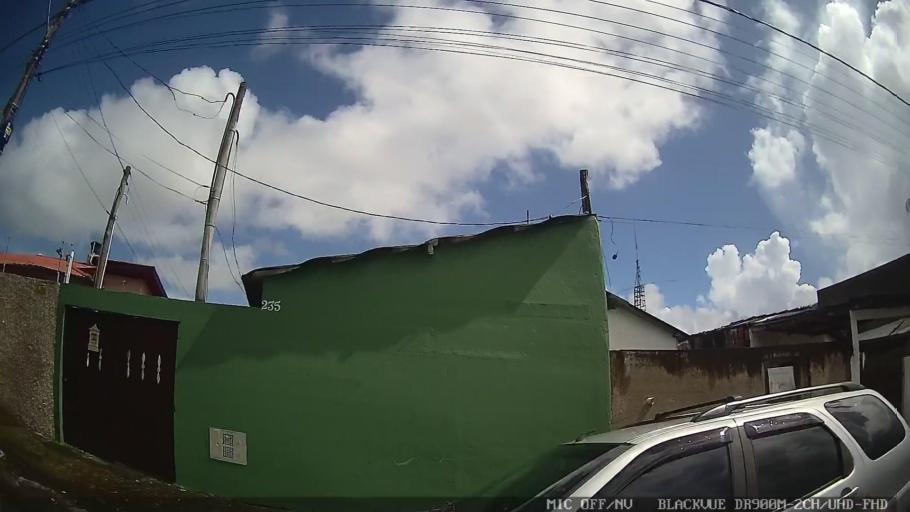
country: BR
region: Sao Paulo
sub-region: Itanhaem
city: Itanhaem
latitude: -24.1904
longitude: -46.8087
